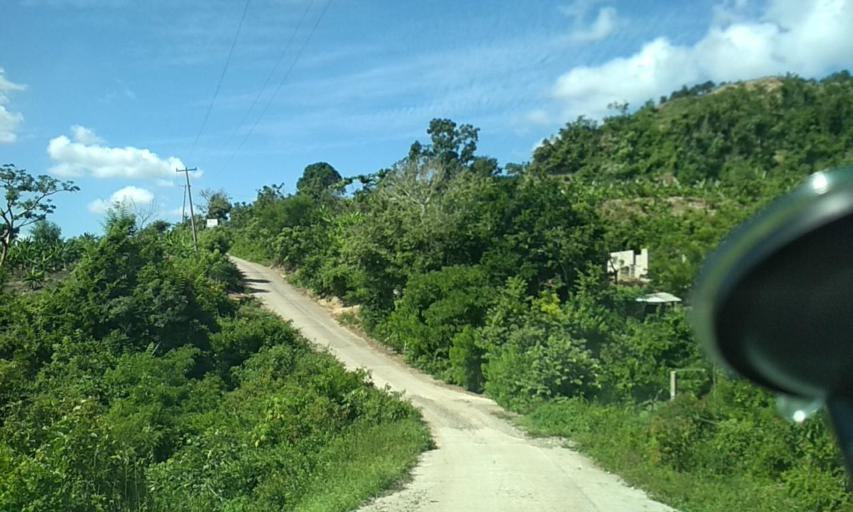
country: MX
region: Veracruz
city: Cazones de Herrera
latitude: 20.6215
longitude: -97.3223
